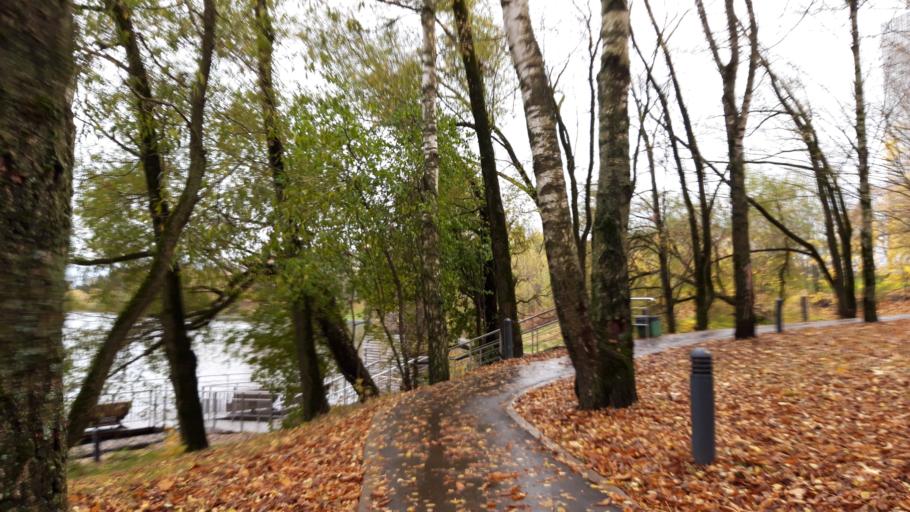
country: RU
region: Moscow
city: Zelenograd
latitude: 55.9865
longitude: 37.2163
